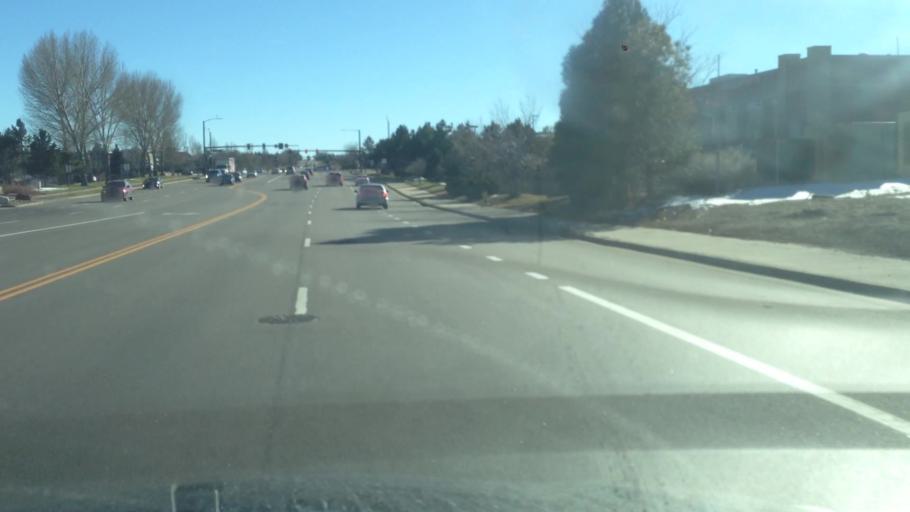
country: US
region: Colorado
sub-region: Douglas County
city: Stonegate
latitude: 39.5361
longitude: -104.7935
